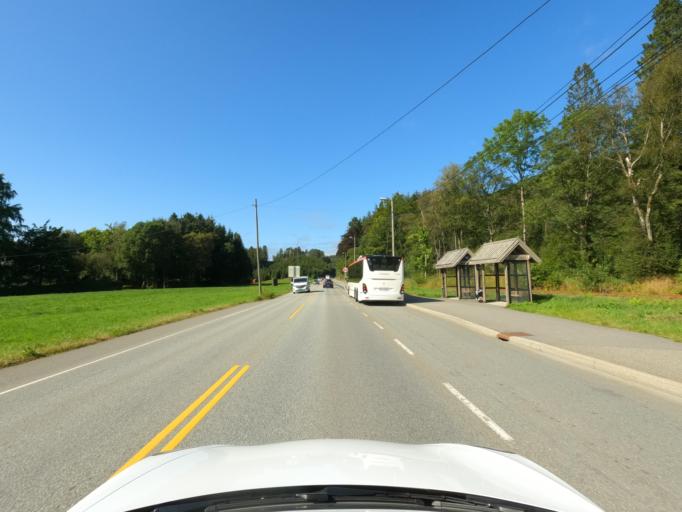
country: NO
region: Hordaland
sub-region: Bergen
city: Sandsli
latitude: 60.2757
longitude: 5.3296
